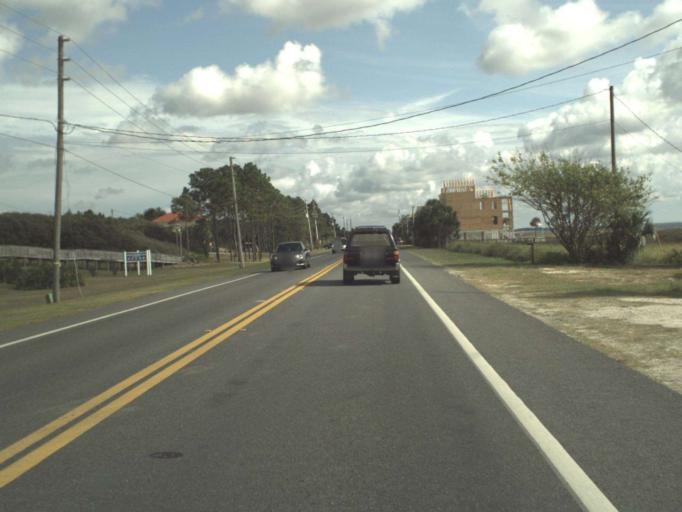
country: US
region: Florida
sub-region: Bay County
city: Mexico Beach
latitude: 29.9177
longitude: -85.3808
